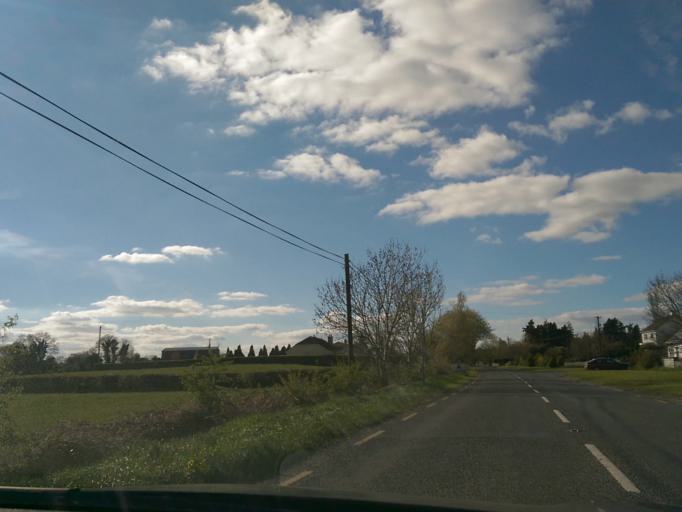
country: IE
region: Leinster
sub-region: Uibh Fhaili
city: Birr
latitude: 53.0871
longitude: -7.9335
